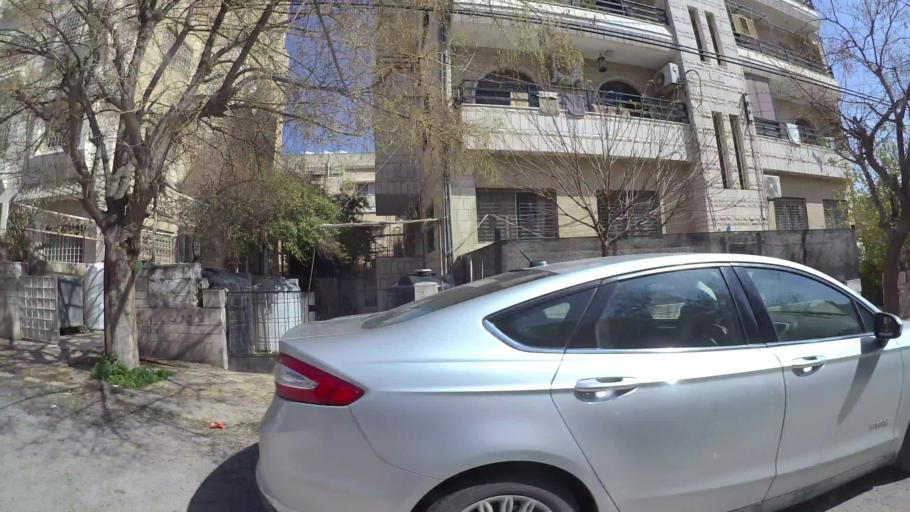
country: JO
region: Amman
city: Amman
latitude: 31.9770
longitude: 35.9859
